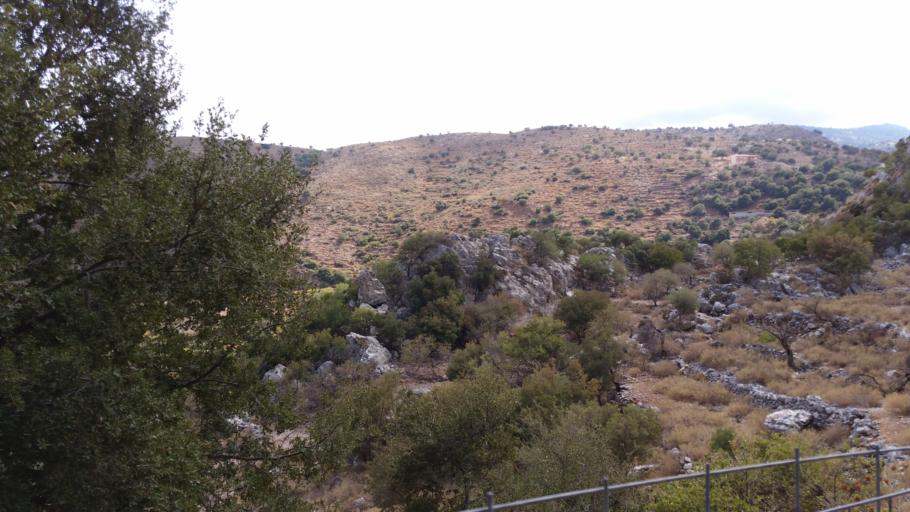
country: GR
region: Crete
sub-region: Nomos Rethymnis
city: Zoniana
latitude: 35.2995
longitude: 24.8402
